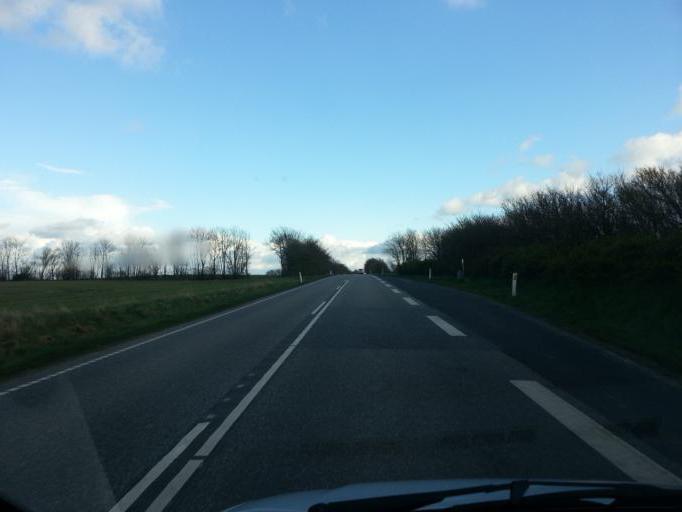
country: DK
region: Central Jutland
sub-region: Ringkobing-Skjern Kommune
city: Tarm
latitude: 55.8675
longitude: 8.5334
